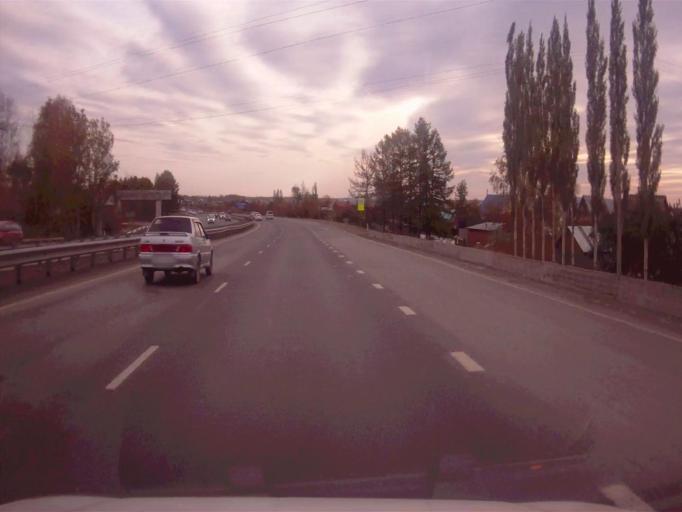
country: RU
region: Chelyabinsk
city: Novosineglazovskiy
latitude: 55.0367
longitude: 61.4416
